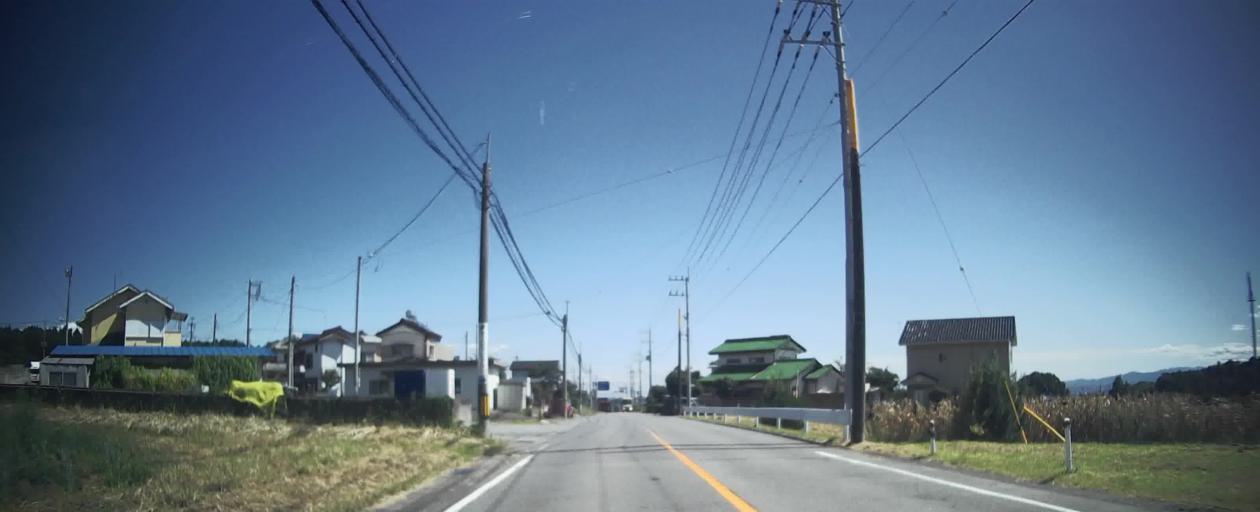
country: JP
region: Gunma
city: Kanekomachi
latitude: 36.4093
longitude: 138.9503
